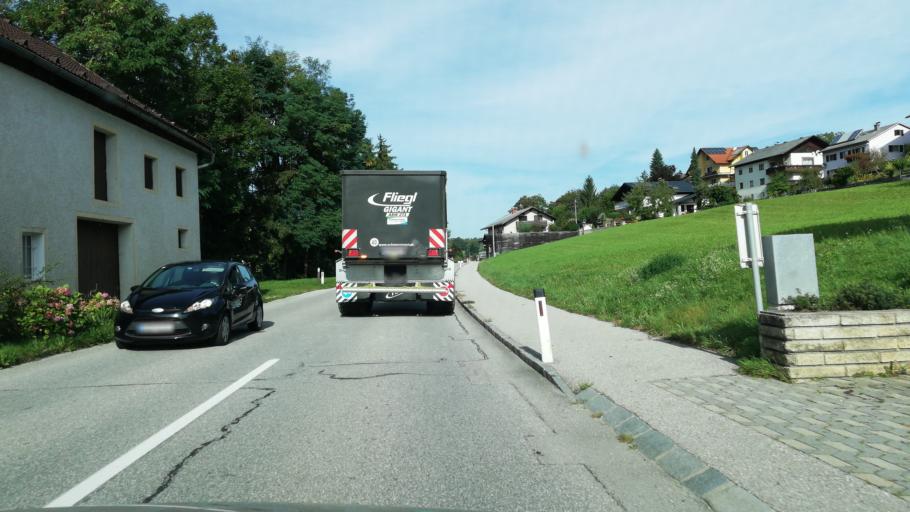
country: AT
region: Lower Austria
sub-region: Politischer Bezirk Amstetten
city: Behamberg
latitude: 48.0206
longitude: 14.4810
